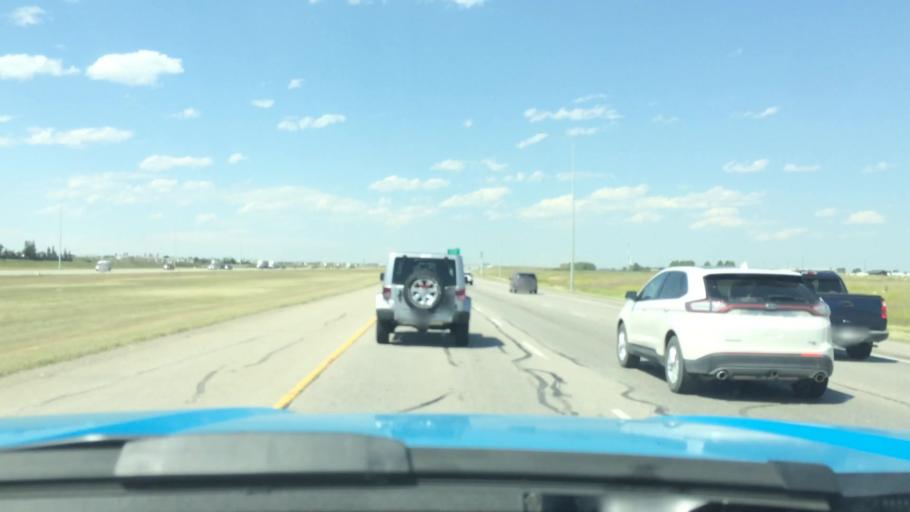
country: CA
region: Alberta
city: Chestermere
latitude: 51.0765
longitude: -113.9200
